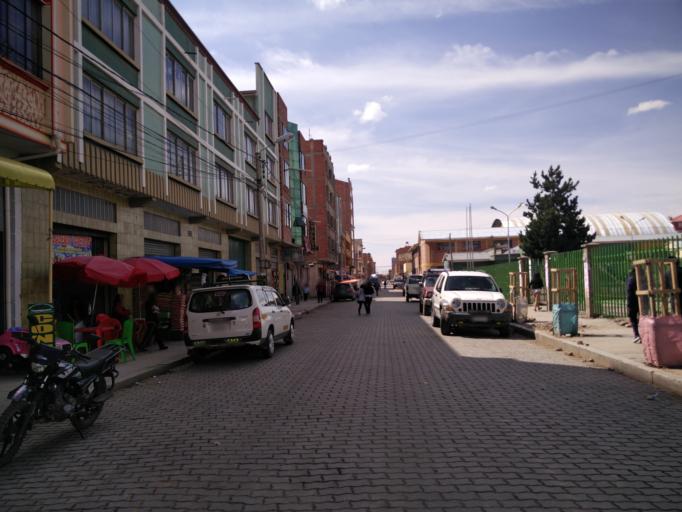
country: BO
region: La Paz
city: La Paz
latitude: -16.5321
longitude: -68.1922
